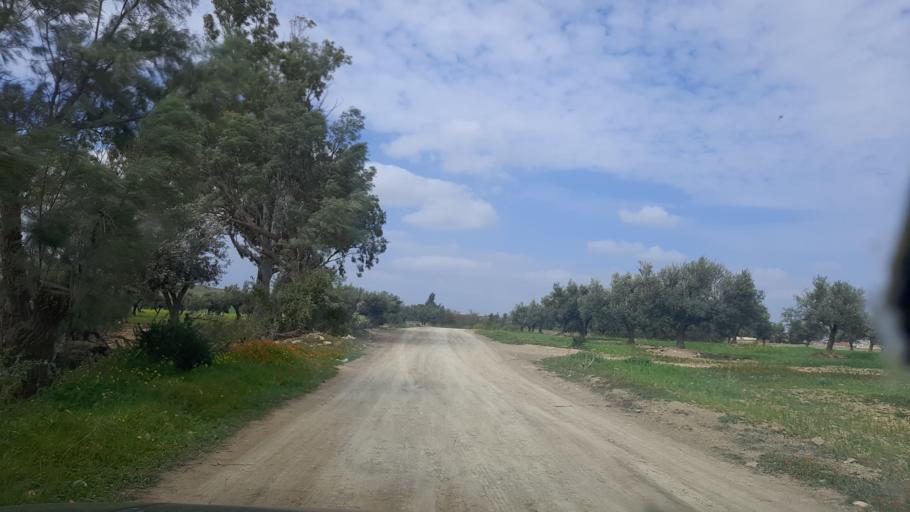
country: TN
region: Tunis
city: Oued Lill
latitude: 36.6890
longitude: 9.9941
